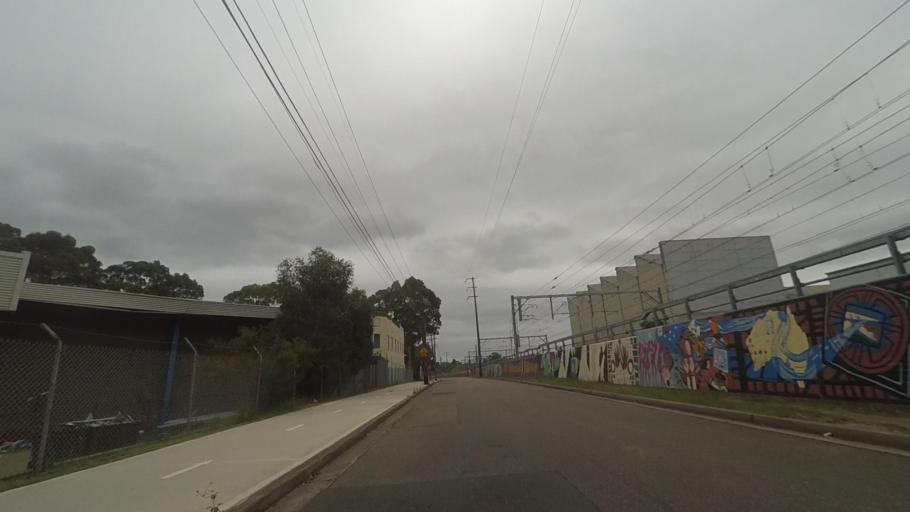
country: AU
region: New South Wales
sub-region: Auburn
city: Auburn
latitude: -33.8543
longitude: 151.0369
